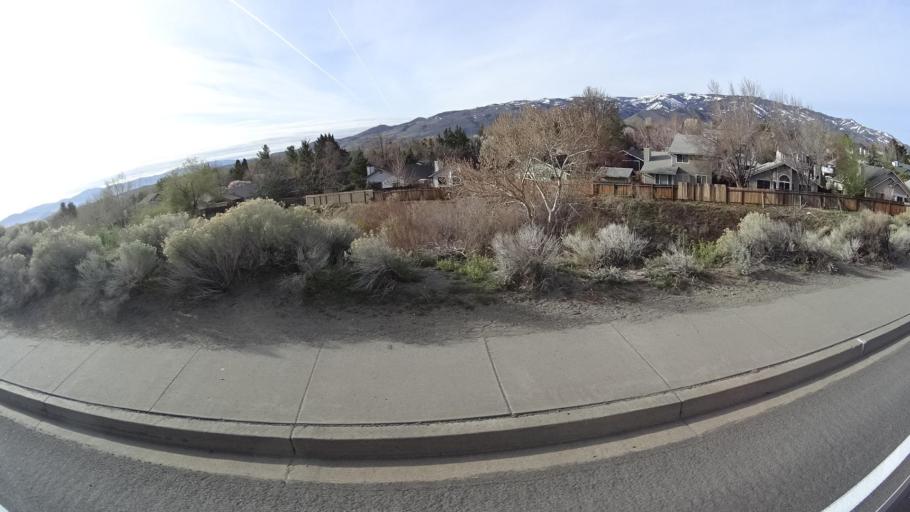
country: US
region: Nevada
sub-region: Washoe County
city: Mogul
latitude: 39.5257
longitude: -119.8908
